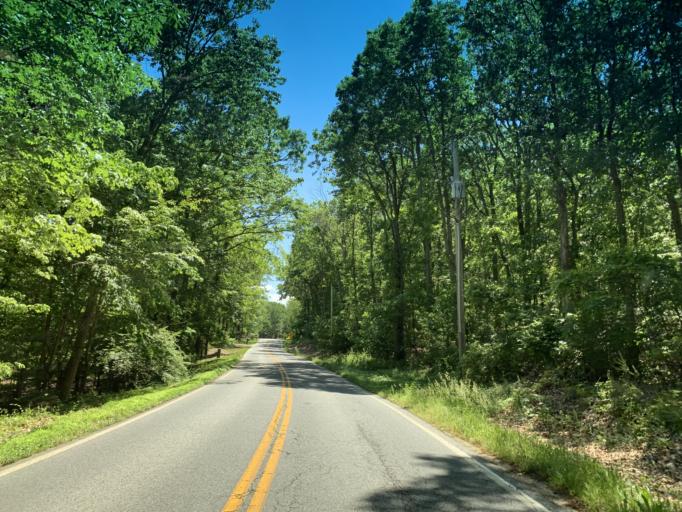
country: US
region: Maryland
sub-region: Cecil County
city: North East
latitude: 39.5516
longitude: -75.9072
